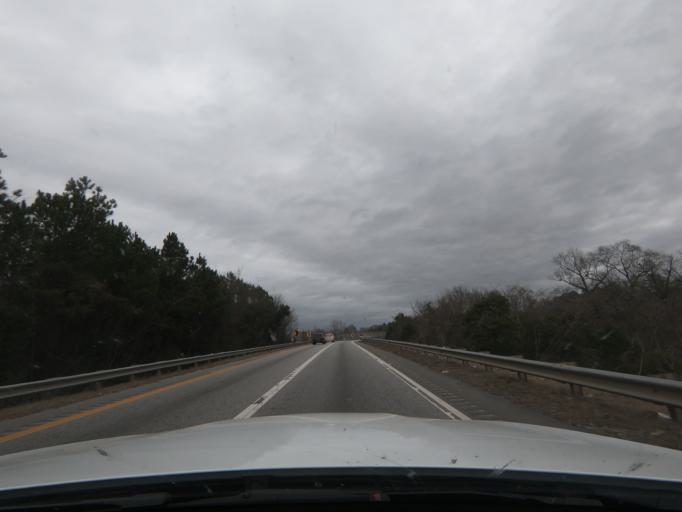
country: US
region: Alabama
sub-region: Russell County
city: Phenix City
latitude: 32.4886
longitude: -85.0315
